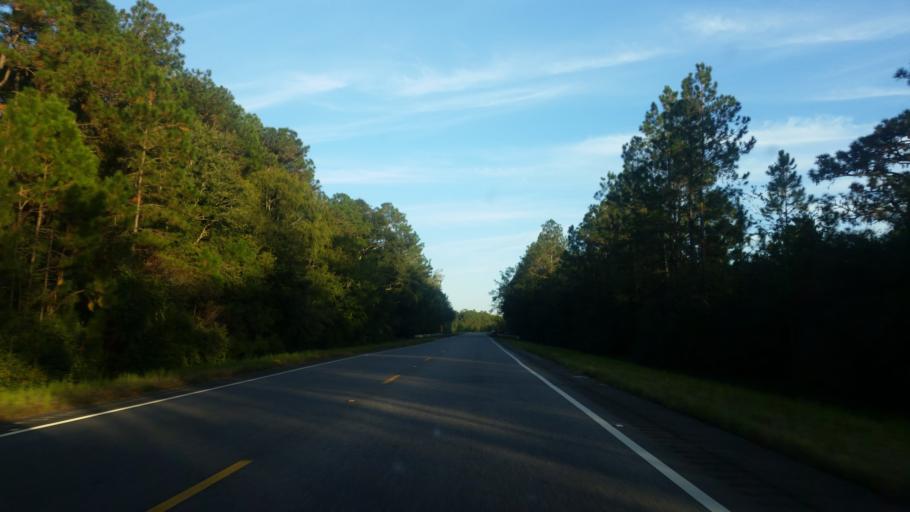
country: US
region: Alabama
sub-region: Mobile County
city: Grand Bay
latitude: 30.4713
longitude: -88.3945
